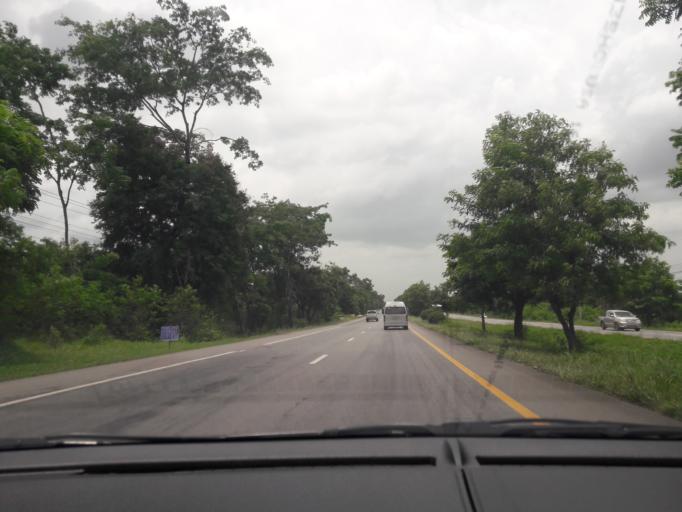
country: TH
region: Nakhon Ratchasima
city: Chaloem Phra Kiat
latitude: 15.0831
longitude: 102.2314
